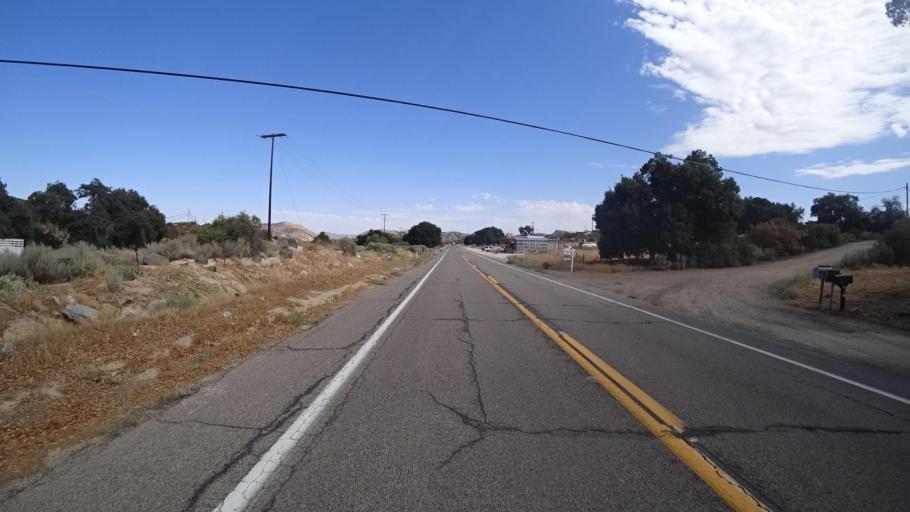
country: MX
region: Baja California
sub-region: Tecate
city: Cereso del Hongo
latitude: 32.6646
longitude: -116.2762
